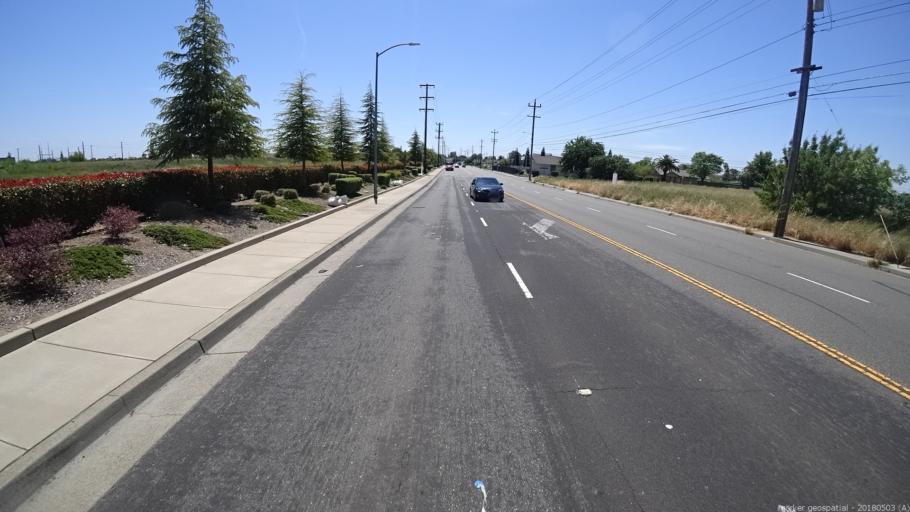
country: US
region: California
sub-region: Sacramento County
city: Arden-Arcade
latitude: 38.6442
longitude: -121.4107
